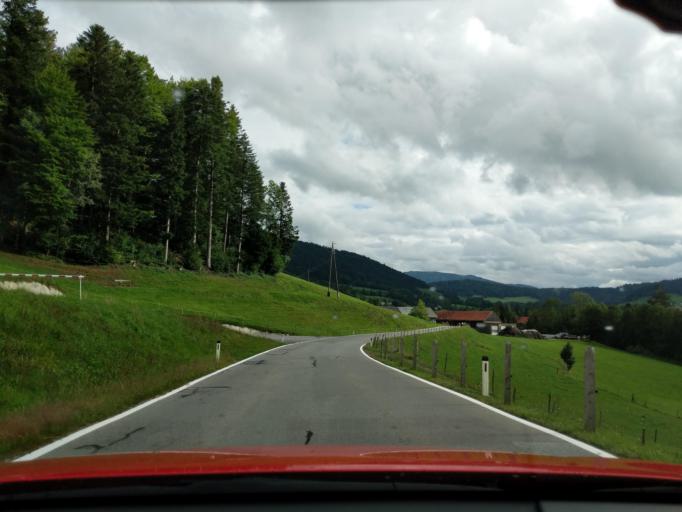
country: AT
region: Vorarlberg
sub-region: Politischer Bezirk Bregenz
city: Riefensberg
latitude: 47.5032
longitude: 9.9461
